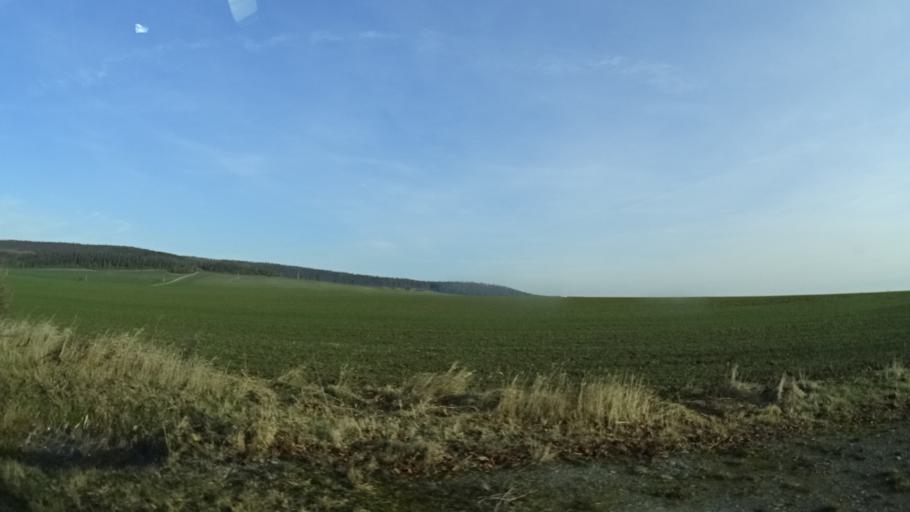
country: DE
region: Thuringia
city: Tonndorf
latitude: 50.8841
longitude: 11.2279
